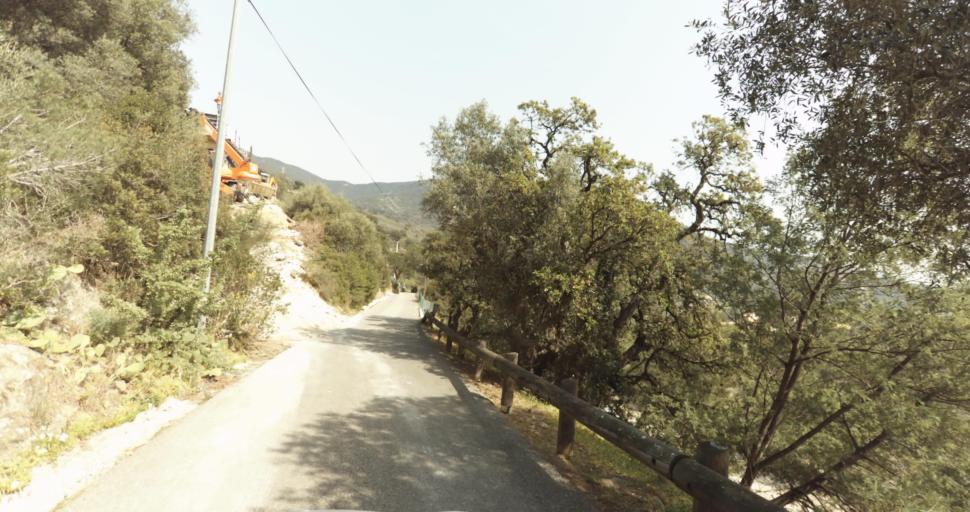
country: FR
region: Provence-Alpes-Cote d'Azur
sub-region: Departement du Var
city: Bormes-les-Mimosas
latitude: 43.1515
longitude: 6.3454
